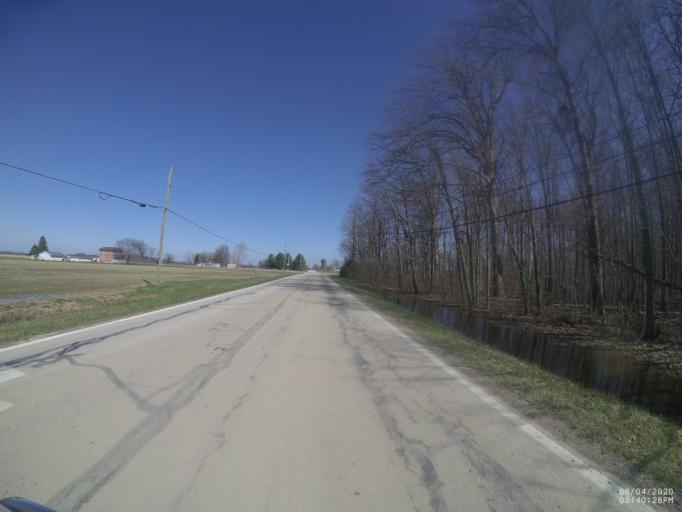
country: US
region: Ohio
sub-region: Sandusky County
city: Stony Prairie
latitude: 41.2675
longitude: -83.2372
